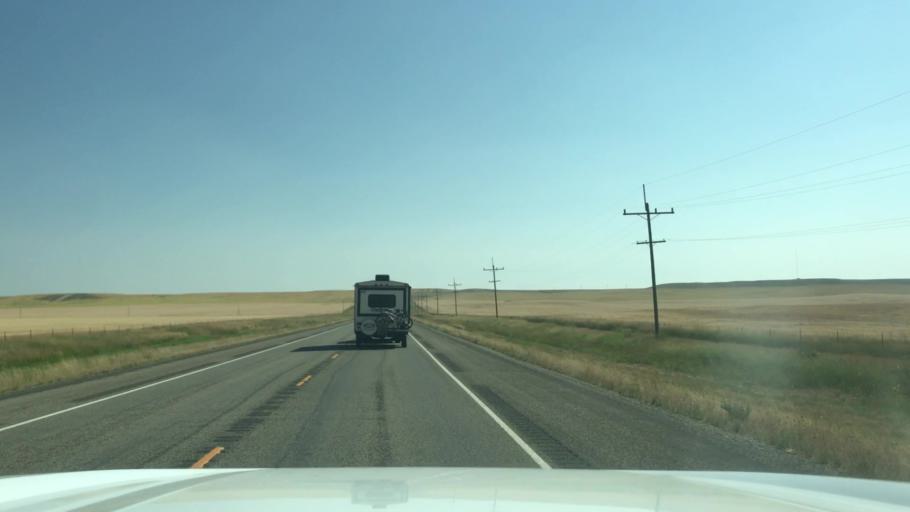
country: US
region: Montana
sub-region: Wheatland County
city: Harlowton
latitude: 46.4852
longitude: -109.7661
